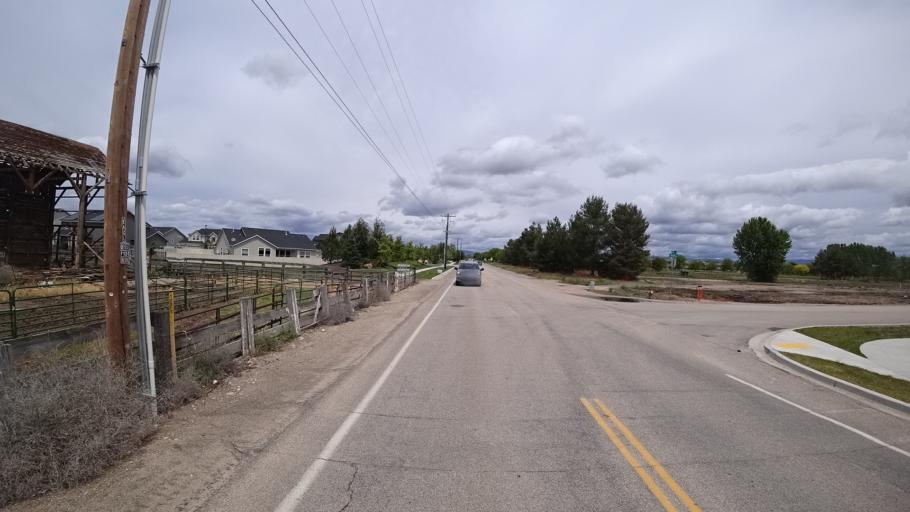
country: US
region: Idaho
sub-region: Ada County
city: Eagle
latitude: 43.6971
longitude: -116.4037
